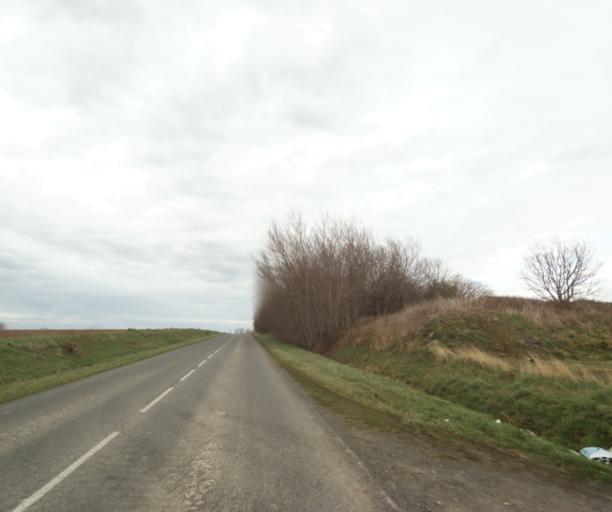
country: FR
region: Nord-Pas-de-Calais
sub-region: Departement du Nord
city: Jenlain
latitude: 50.3262
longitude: 3.6331
